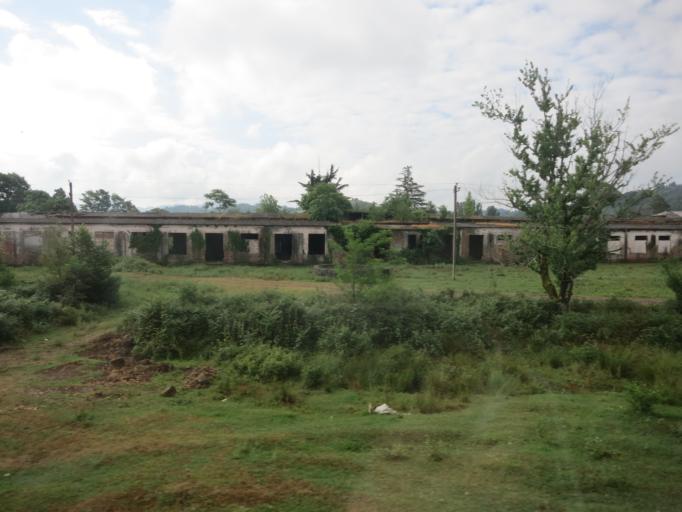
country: GE
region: Guria
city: Lanchkhuti
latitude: 42.0782
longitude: 41.9159
